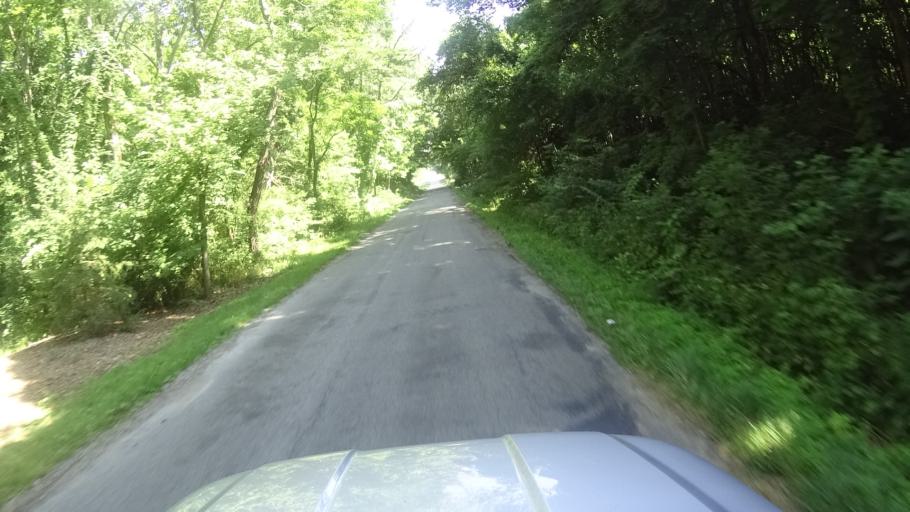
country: US
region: Indiana
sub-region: Madison County
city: Ingalls
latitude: 39.9602
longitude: -85.8150
